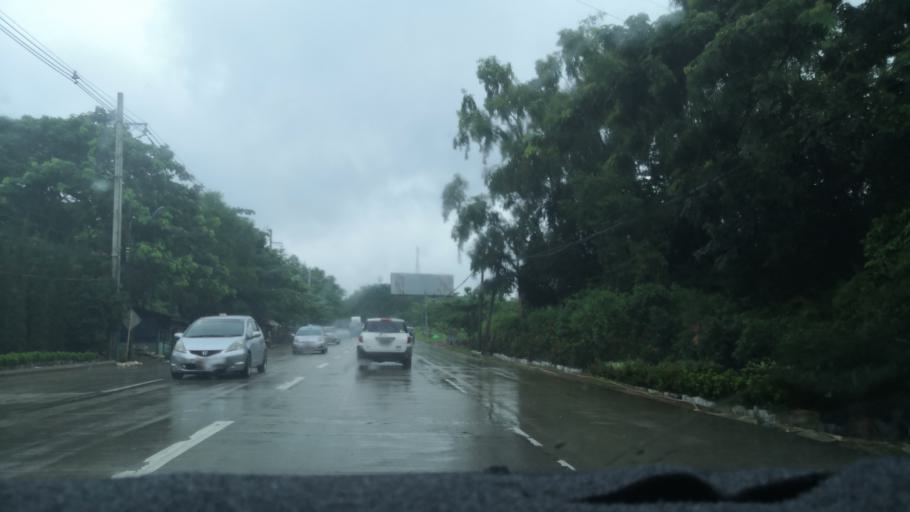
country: MM
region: Yangon
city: Yangon
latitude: 16.8889
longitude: 96.1486
